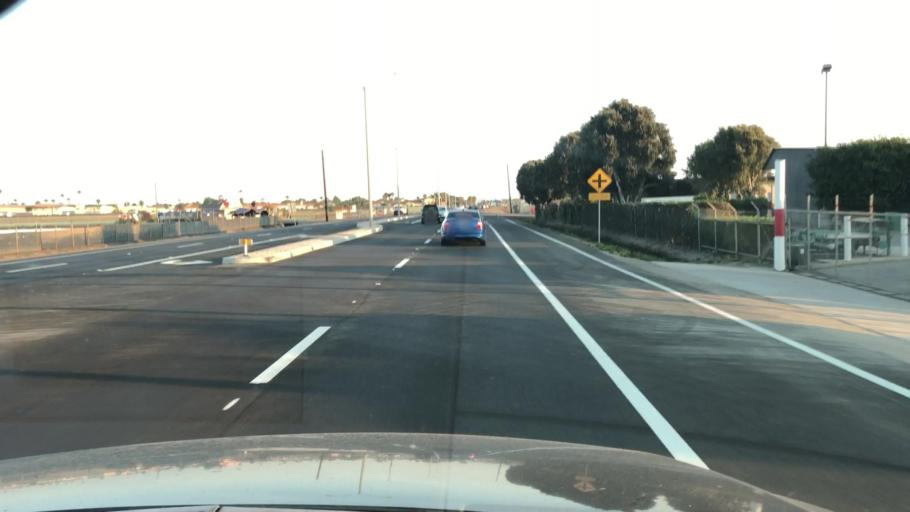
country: US
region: California
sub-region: Ventura County
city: Oxnard Shores
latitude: 34.2043
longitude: -119.2211
